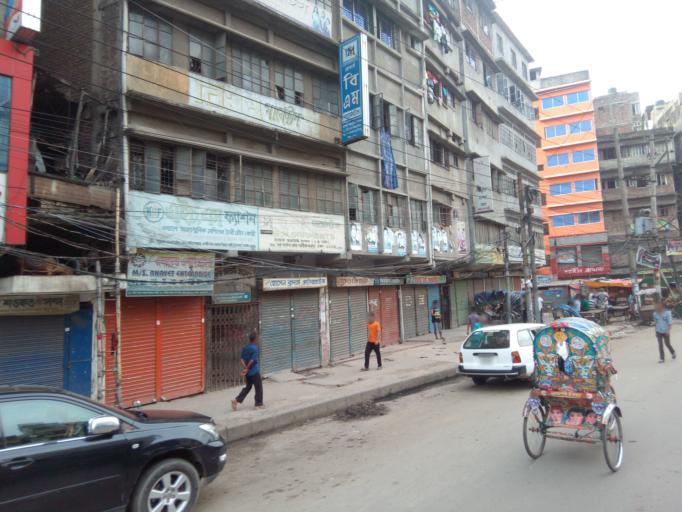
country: BD
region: Dhaka
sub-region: Dhaka
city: Dhaka
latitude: 23.7185
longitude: 90.4087
